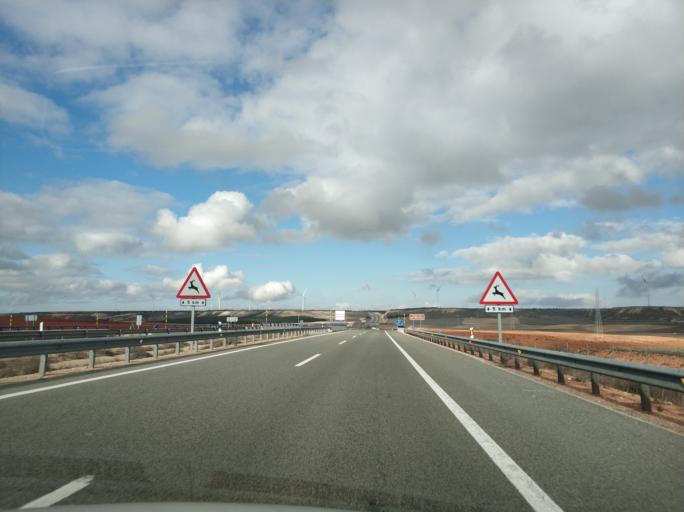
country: ES
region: Castille and Leon
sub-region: Provincia de Soria
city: Alcubilla de las Penas
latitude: 41.2689
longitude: -2.4742
